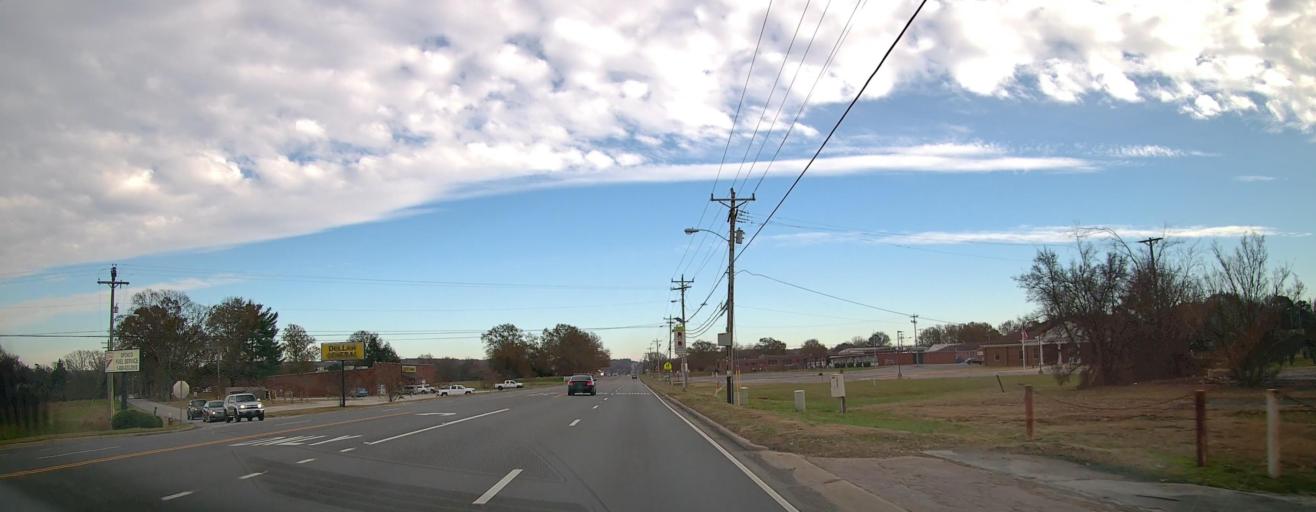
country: US
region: Alabama
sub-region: Morgan County
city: Priceville
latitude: 34.5296
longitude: -86.9010
